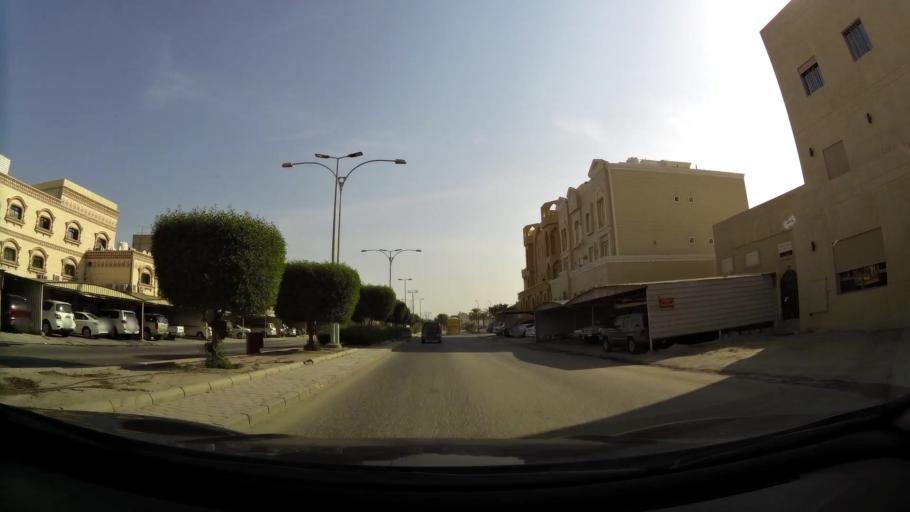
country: KW
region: Al Ahmadi
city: Ar Riqqah
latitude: 29.1453
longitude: 48.1066
